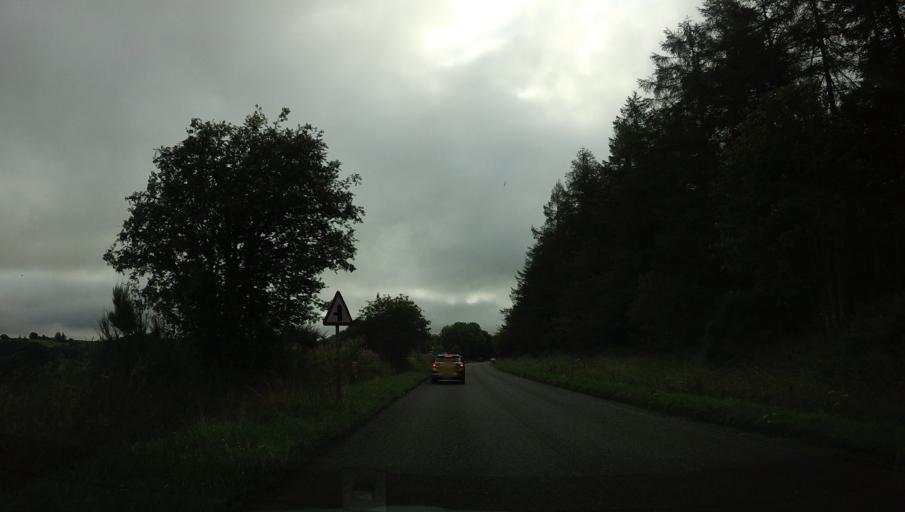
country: GB
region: Scotland
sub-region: Aberdeenshire
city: Westhill
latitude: 57.1022
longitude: -2.2940
